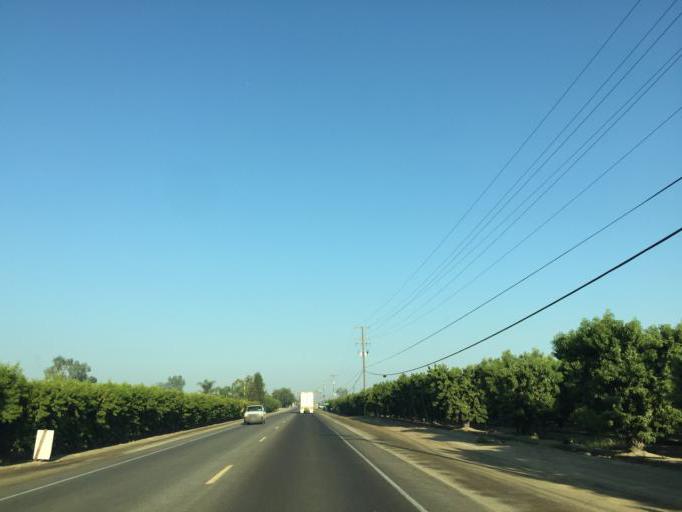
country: US
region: California
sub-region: Fresno County
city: Kingsburg
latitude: 36.4888
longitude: -119.5082
